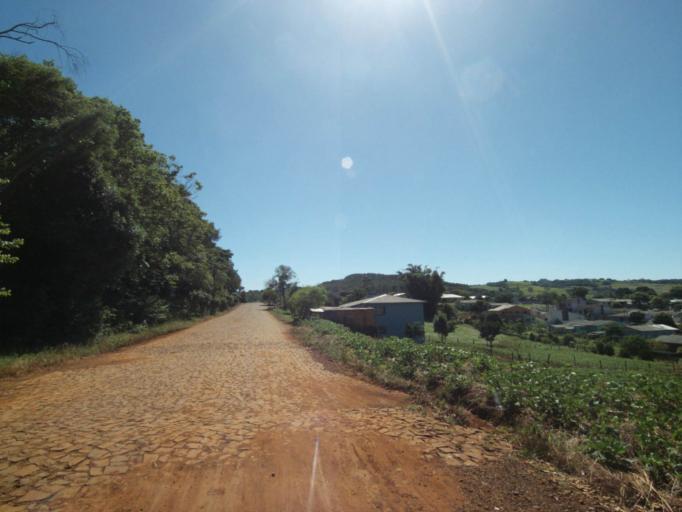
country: BR
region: Santa Catarina
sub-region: Sao Lourenco Do Oeste
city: Sao Lourenco dOeste
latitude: -26.2691
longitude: -52.7836
